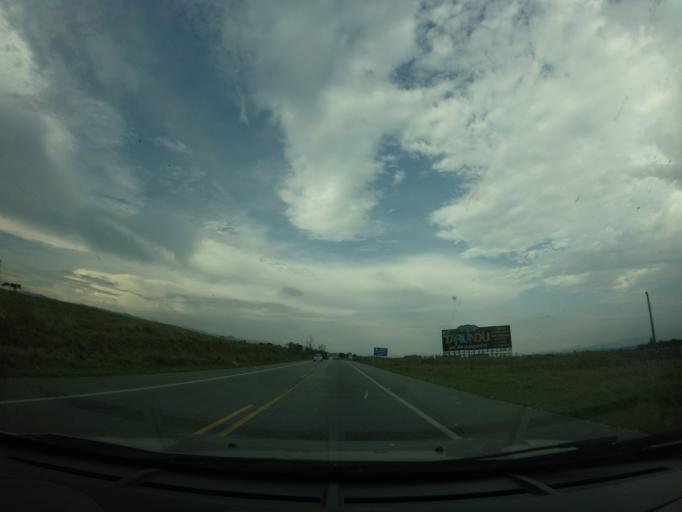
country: BR
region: Sao Paulo
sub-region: Tremembe
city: Tremembe
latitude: -22.9413
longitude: -45.6004
